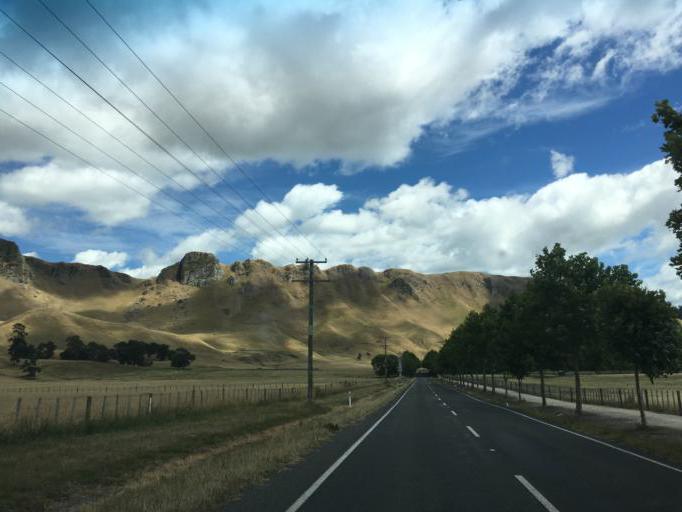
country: NZ
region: Hawke's Bay
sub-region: Hastings District
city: Hastings
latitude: -39.6988
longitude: 176.9255
